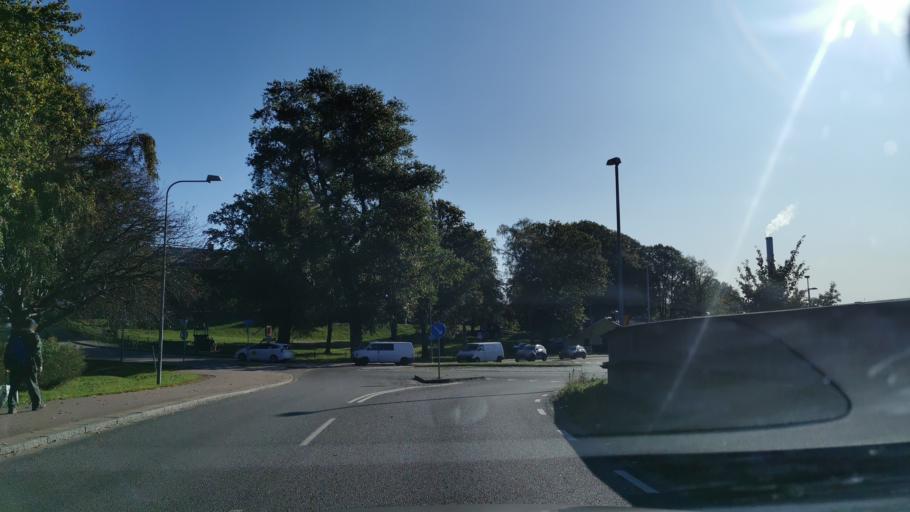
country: SE
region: Vaestra Goetaland
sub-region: Goteborg
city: Eriksbo
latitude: 57.7356
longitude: 12.0280
